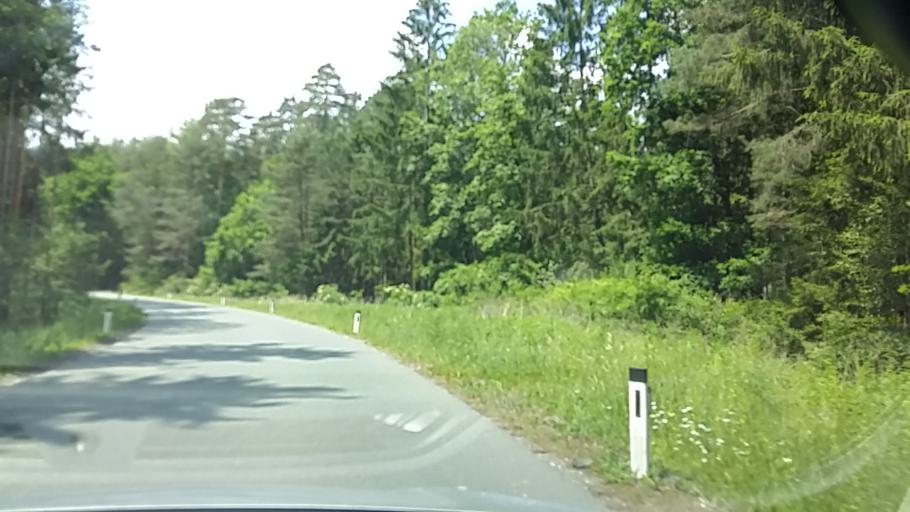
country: AT
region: Styria
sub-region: Politischer Bezirk Hartberg-Fuerstenfeld
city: Burgau
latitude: 47.1201
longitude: 16.0881
